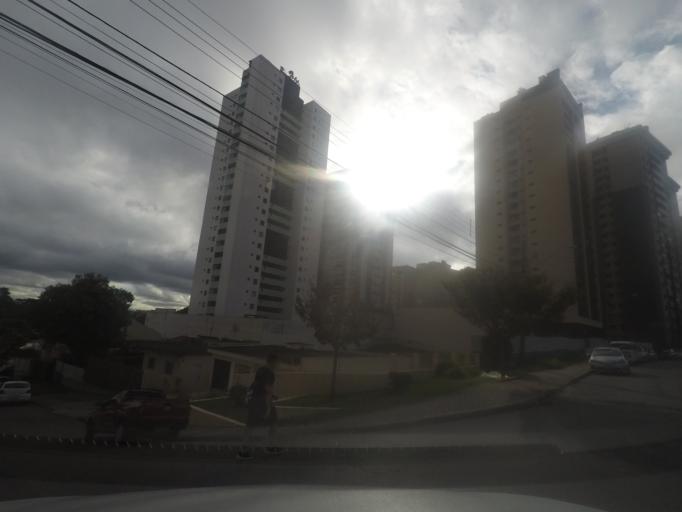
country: BR
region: Parana
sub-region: Curitiba
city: Curitiba
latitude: -25.4403
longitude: -49.2357
